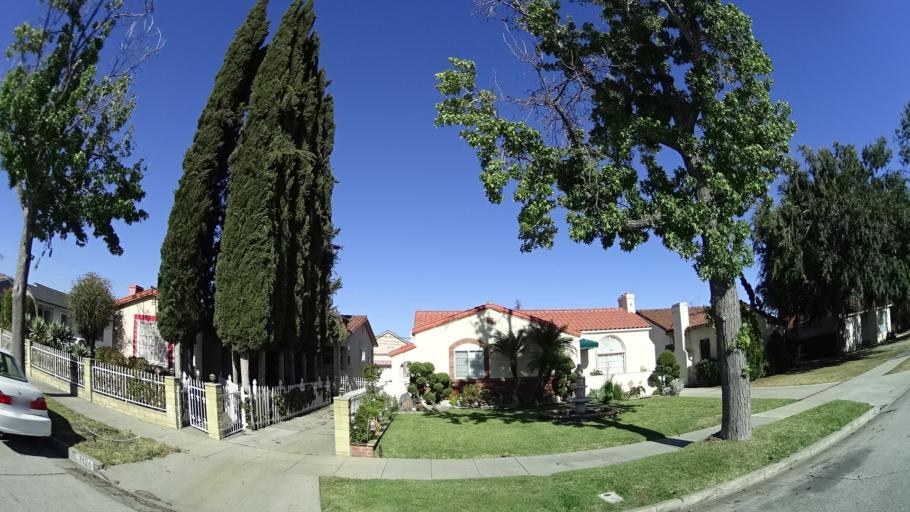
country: US
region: California
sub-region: Los Angeles County
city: Monterey Park
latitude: 34.0762
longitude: -118.1444
